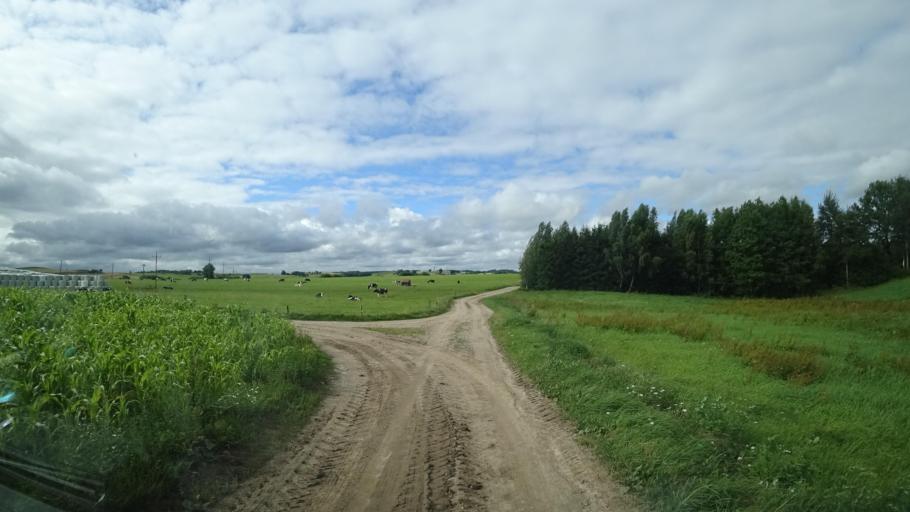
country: PL
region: Podlasie
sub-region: Suwalki
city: Suwalki
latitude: 54.3733
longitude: 22.9019
